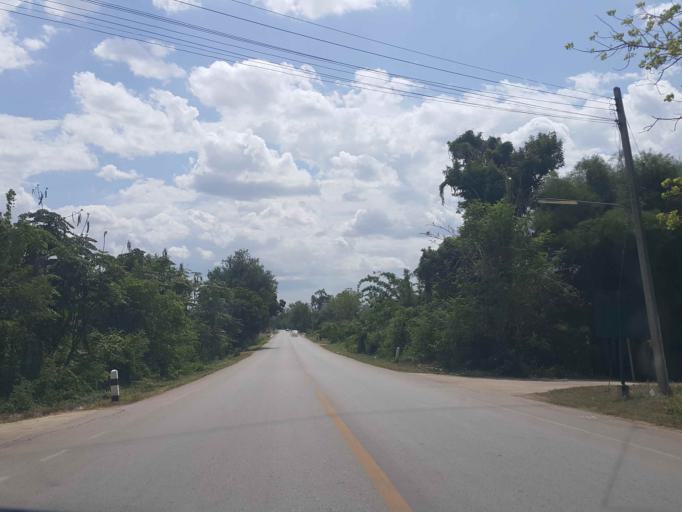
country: TH
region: Sukhothai
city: Thung Saliam
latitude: 17.3369
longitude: 99.5874
